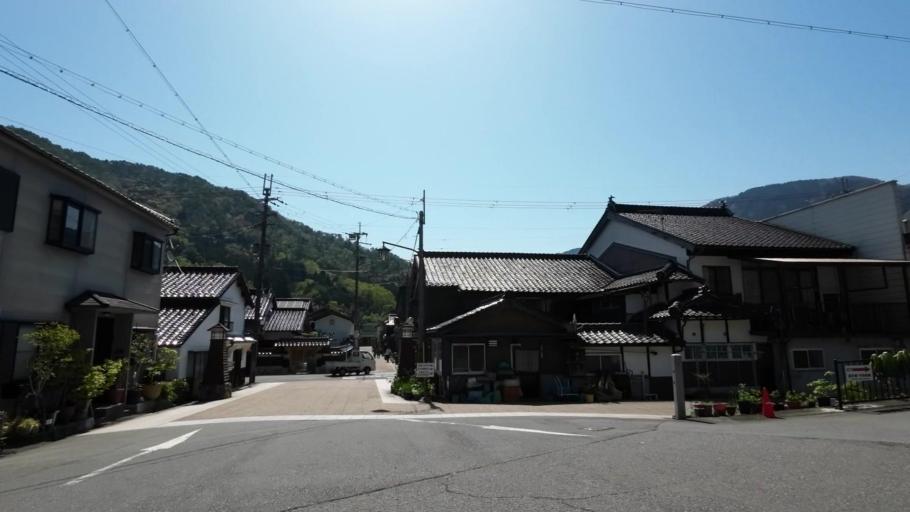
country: JP
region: Hyogo
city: Toyooka
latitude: 35.2990
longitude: 134.8361
